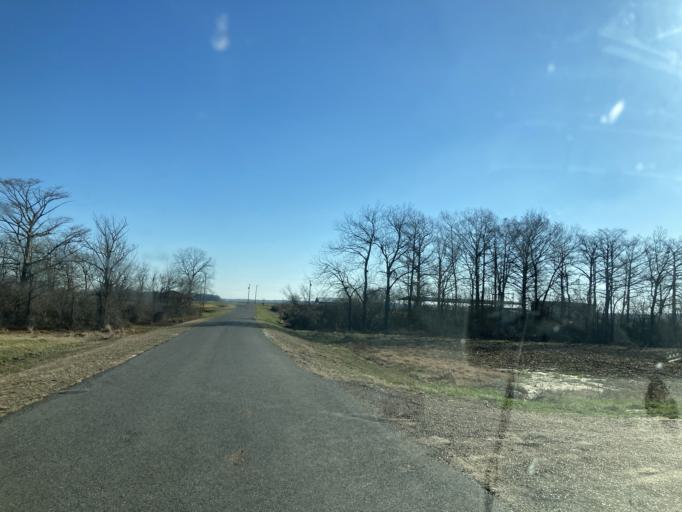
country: US
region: Mississippi
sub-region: Yazoo County
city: Yazoo City
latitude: 32.9519
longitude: -90.5936
